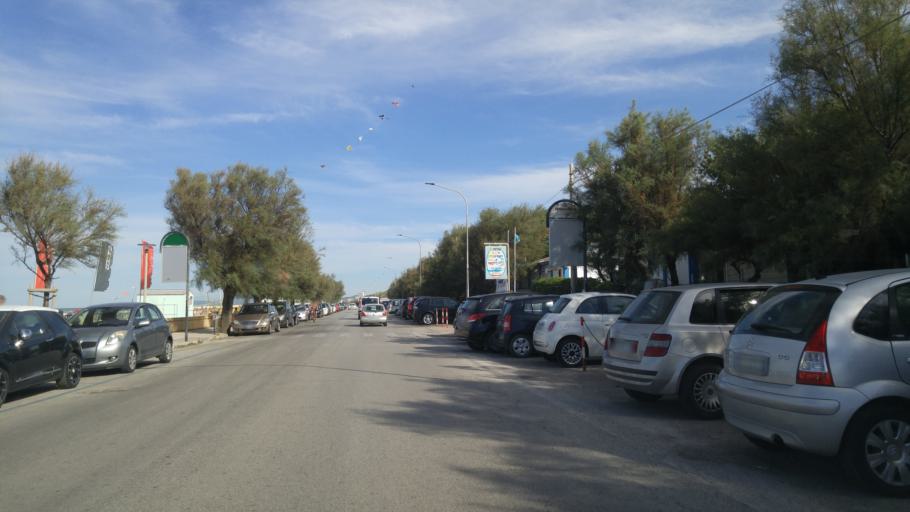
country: IT
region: The Marches
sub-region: Provincia di Ancona
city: Montignano-Marzocca
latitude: 43.6902
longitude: 13.2650
